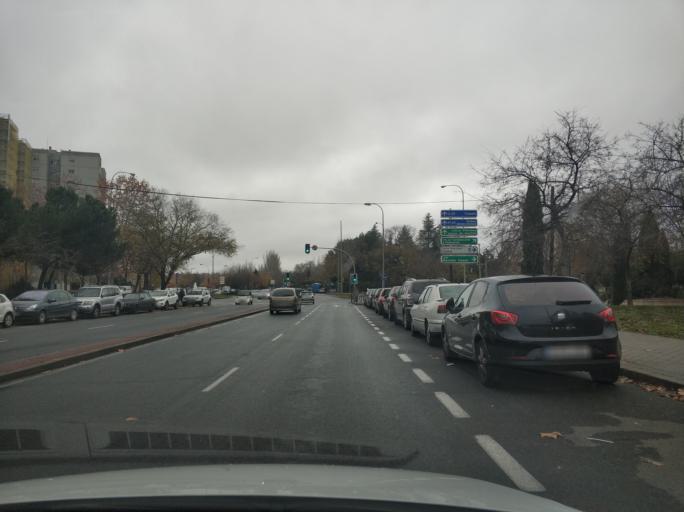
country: ES
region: Madrid
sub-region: Provincia de Madrid
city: Usera
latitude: 40.3731
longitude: -3.7111
